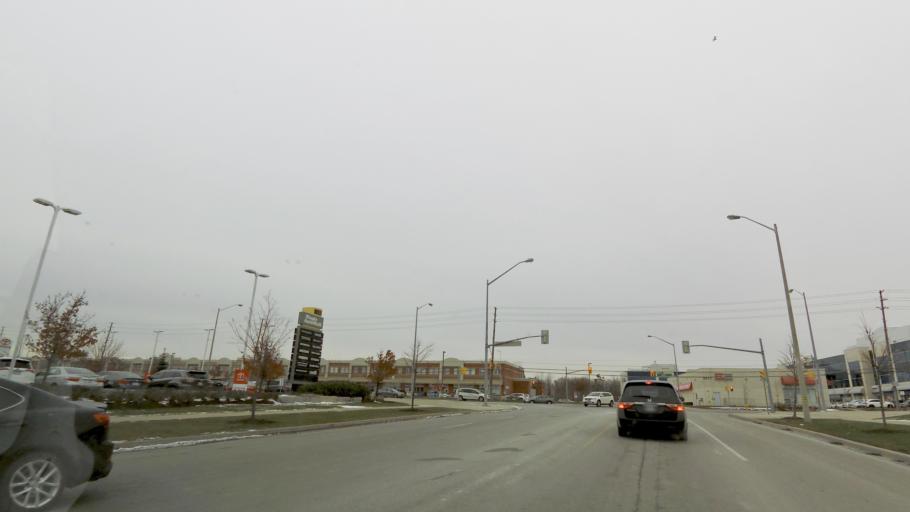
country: CA
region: Ontario
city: Vaughan
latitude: 43.8357
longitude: -79.5345
